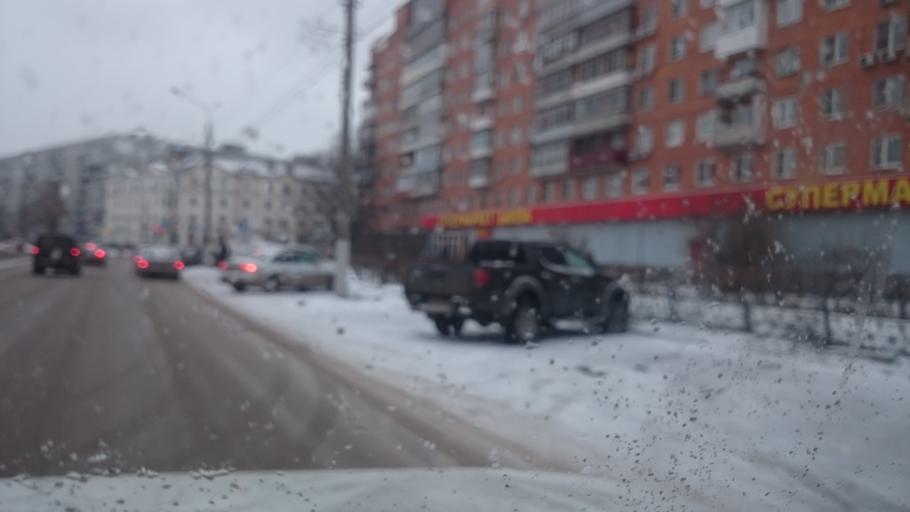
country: RU
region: Tula
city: Tula
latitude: 54.1982
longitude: 37.6014
